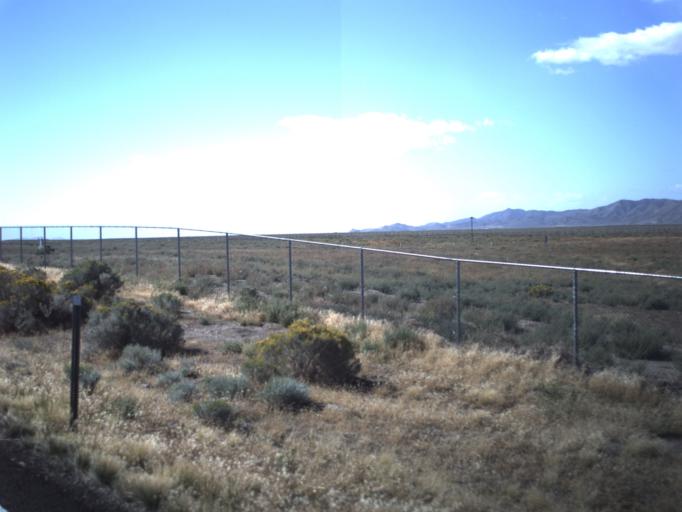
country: US
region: Utah
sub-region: Beaver County
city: Milford
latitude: 38.4384
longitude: -113.0098
